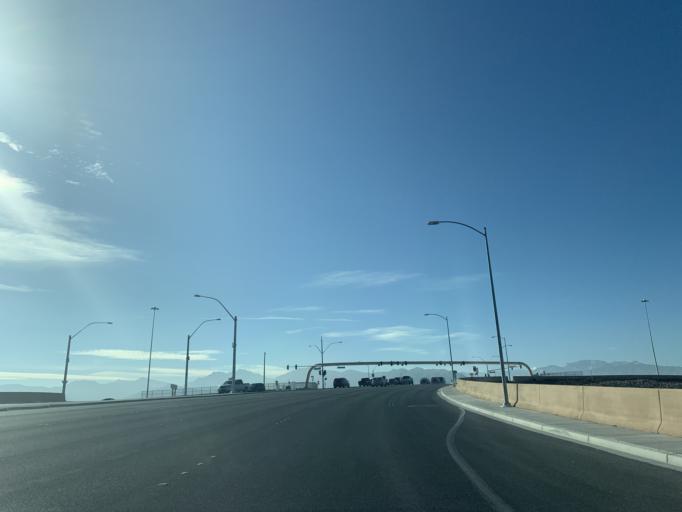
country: US
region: Nevada
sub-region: Clark County
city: Summerlin South
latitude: 36.3150
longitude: -115.2986
